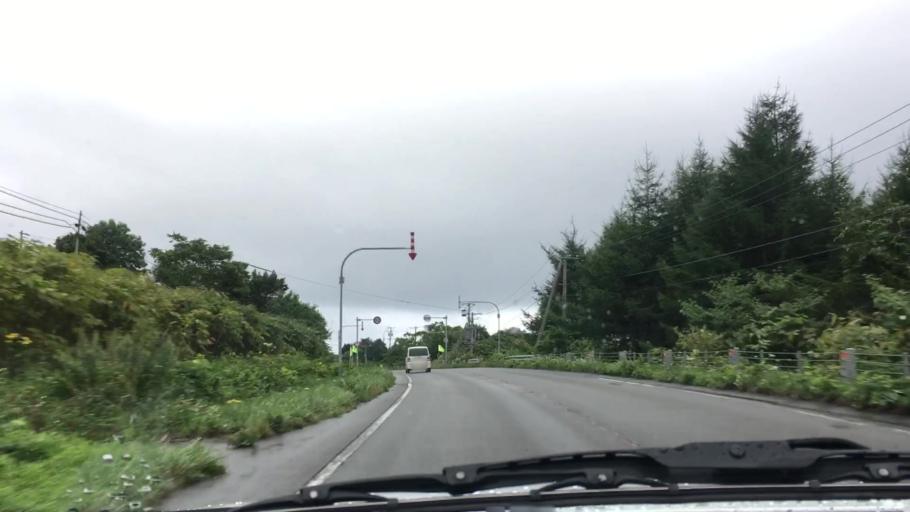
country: JP
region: Hokkaido
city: Niseko Town
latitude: 42.6015
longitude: 140.7240
